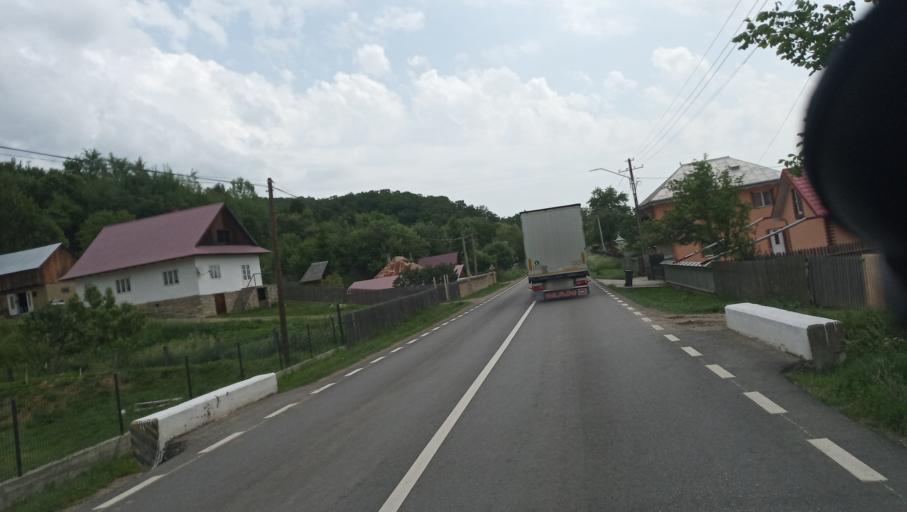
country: RO
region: Neamt
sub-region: Comuna Pipirig
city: Stanca
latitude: 47.2237
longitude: 26.1915
